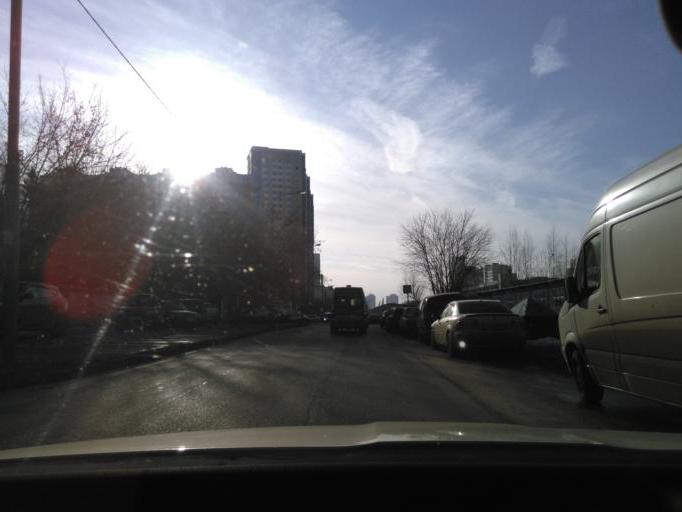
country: RU
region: Moskovskaya
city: Levoberezhnaya
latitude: 55.8730
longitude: 37.4725
